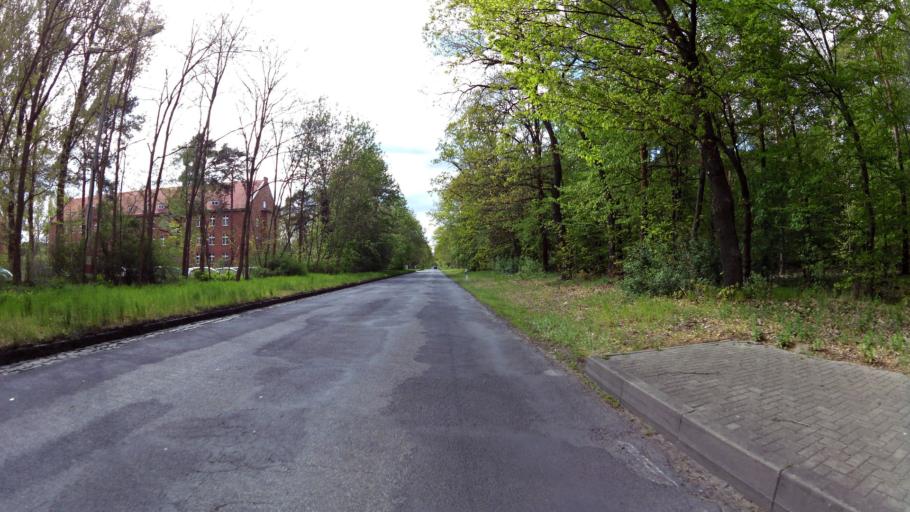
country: DE
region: Brandenburg
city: Furstenwalde
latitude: 52.3589
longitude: 14.0427
